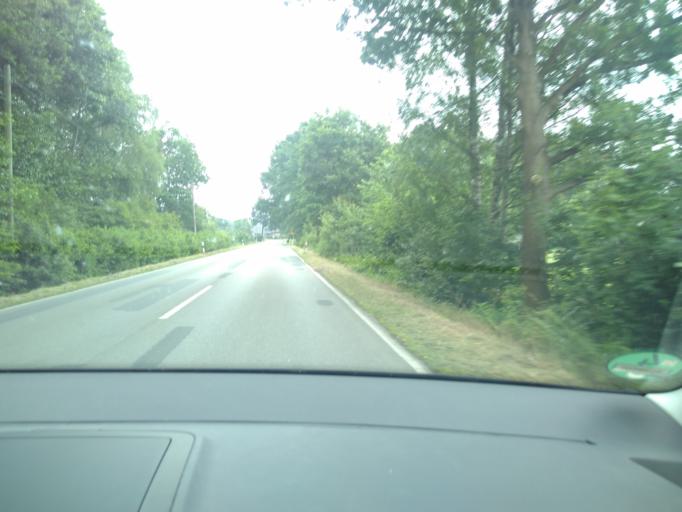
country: DE
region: North Rhine-Westphalia
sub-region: Regierungsbezirk Detmold
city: Steinhagen
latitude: 51.9551
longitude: 8.4711
